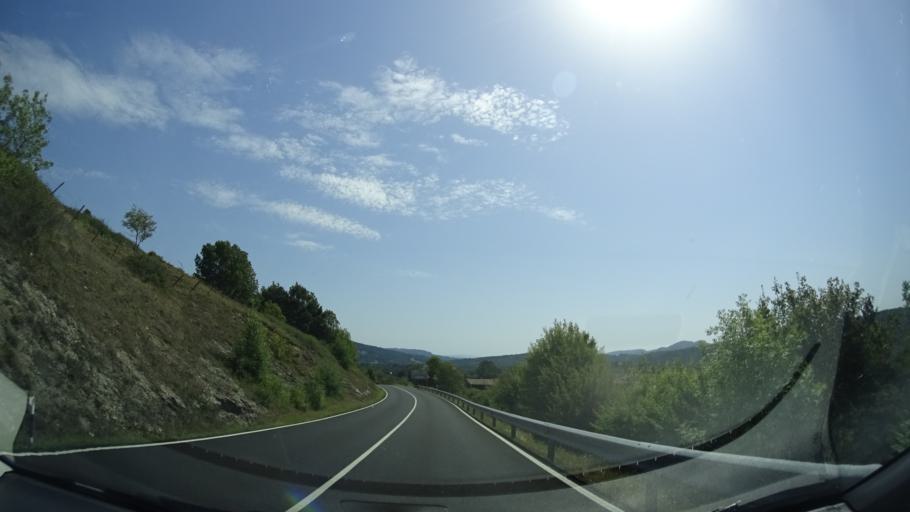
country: ES
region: Basque Country
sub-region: Provincia de Alava
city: Murguia
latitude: 42.9614
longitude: -2.8886
